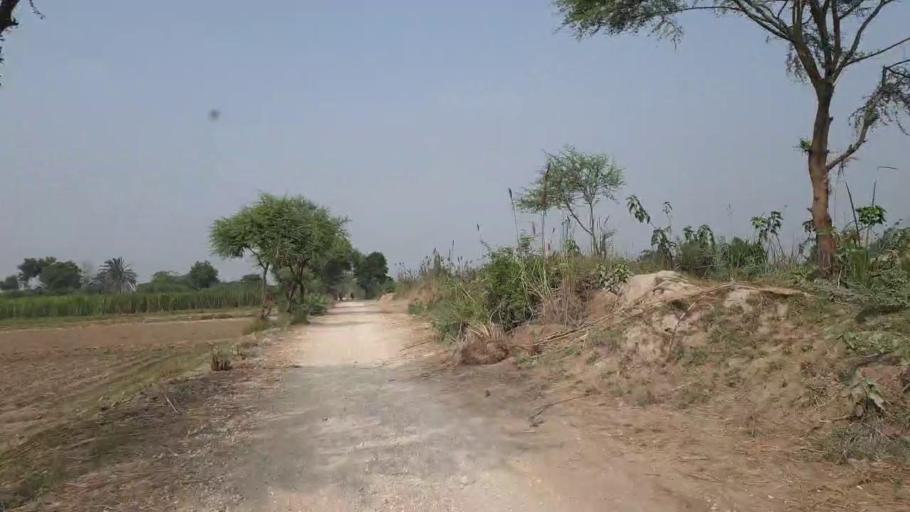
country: PK
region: Sindh
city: Matli
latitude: 25.0229
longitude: 68.5976
